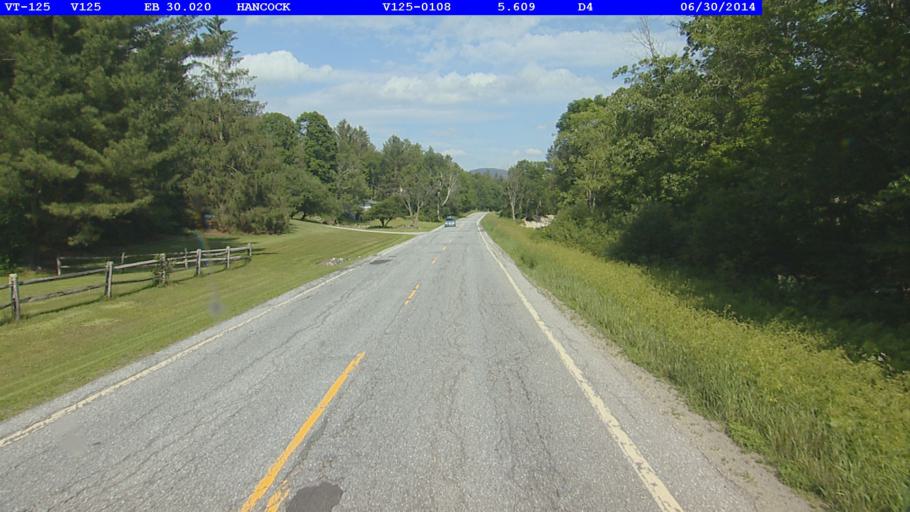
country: US
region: Vermont
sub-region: Orange County
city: Randolph
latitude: 43.9268
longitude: -72.8713
